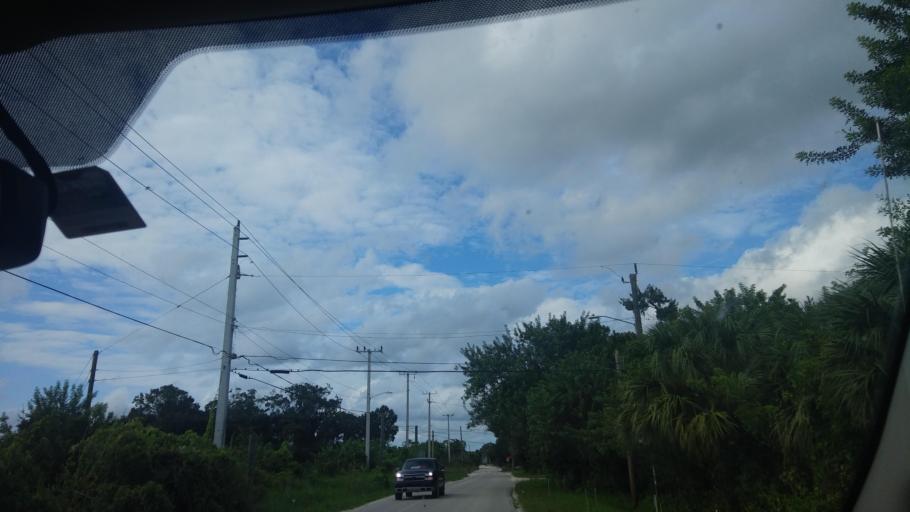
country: US
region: Florida
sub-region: Indian River County
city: Fellsmere
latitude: 27.7781
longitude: -80.5930
